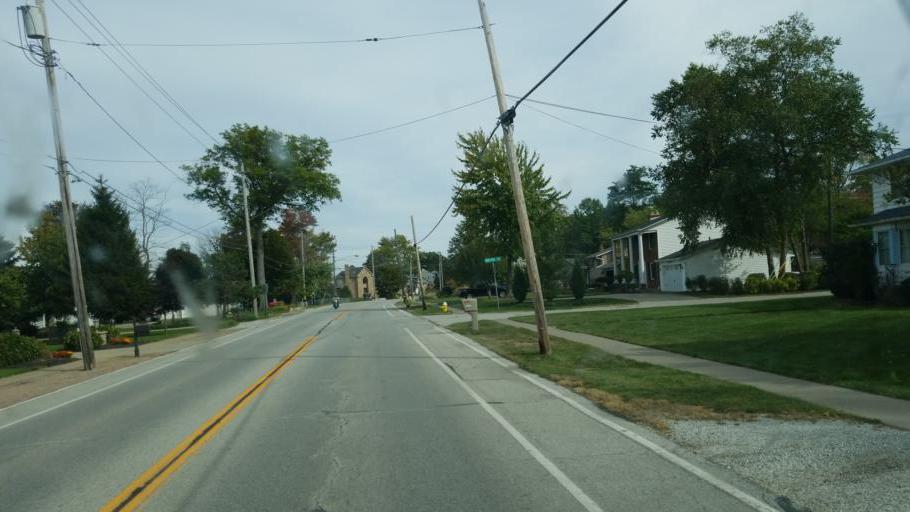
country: US
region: Ohio
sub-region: Lorain County
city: Avon Lake
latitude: 41.5138
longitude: -82.0040
